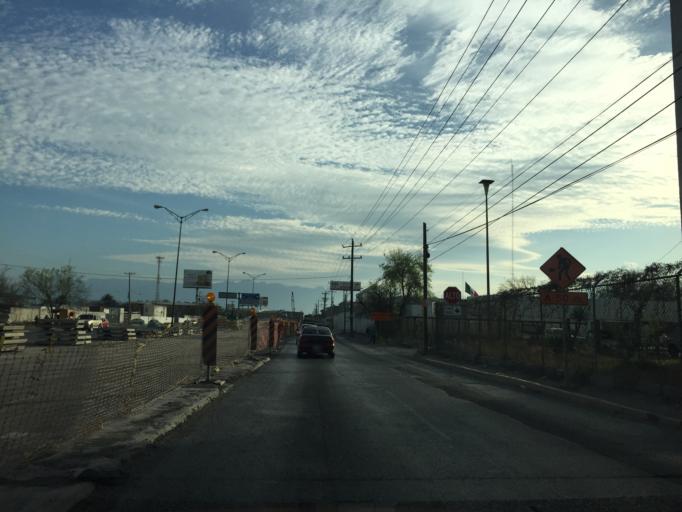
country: MX
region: Nuevo Leon
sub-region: Apodaca
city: Fraccionamiento Cosmopolis Octavo Sector
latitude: 25.8070
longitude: -100.2745
